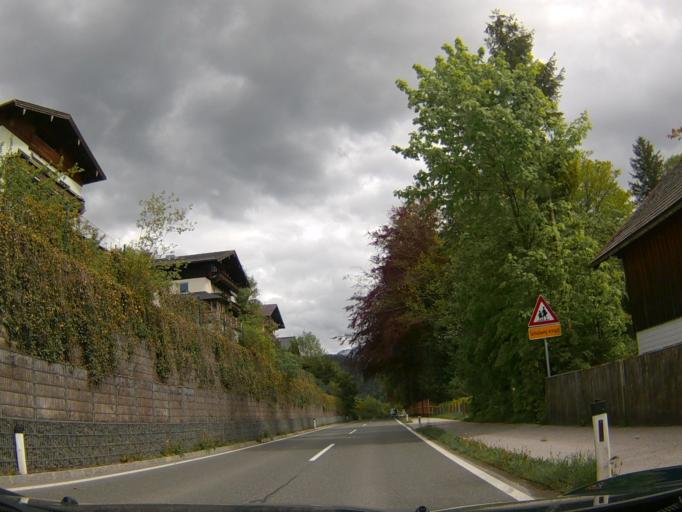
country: AT
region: Upper Austria
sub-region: Politischer Bezirk Gmunden
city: Sankt Wolfgang im Salzkammergut
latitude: 47.7347
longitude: 13.4587
